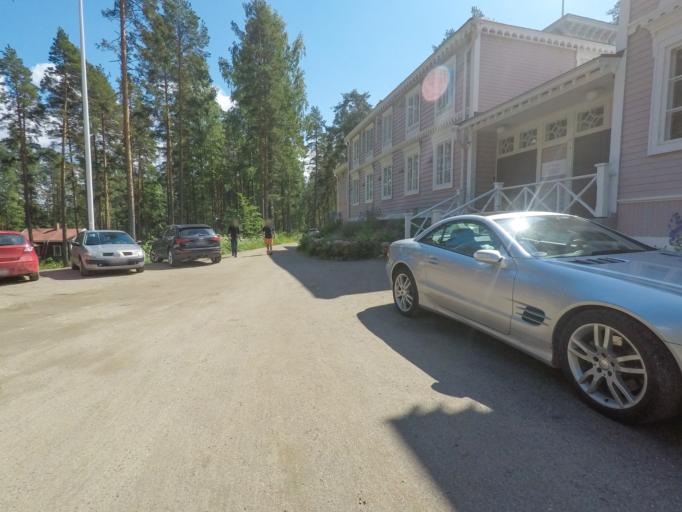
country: FI
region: Southern Savonia
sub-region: Savonlinna
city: Punkaharju
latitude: 61.8011
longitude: 29.3078
